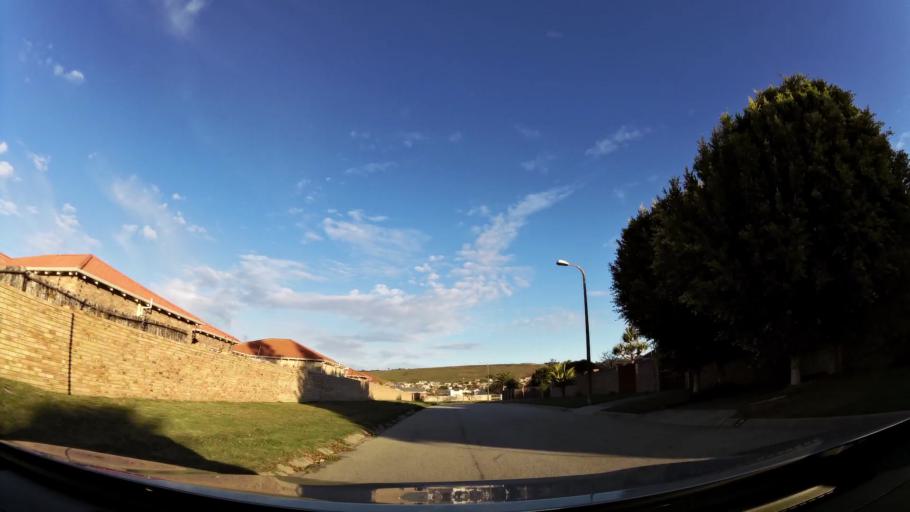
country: ZA
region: Eastern Cape
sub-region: Nelson Mandela Bay Metropolitan Municipality
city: Port Elizabeth
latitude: -33.9765
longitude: 25.4934
